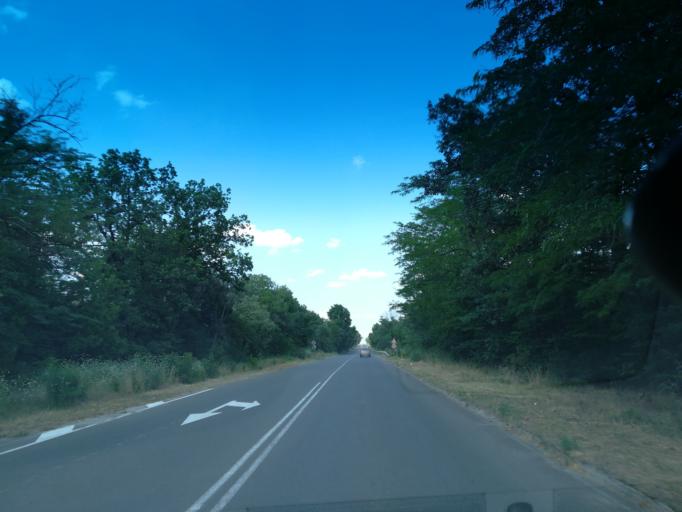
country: BG
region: Stara Zagora
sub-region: Obshtina Chirpan
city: Chirpan
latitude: 42.2040
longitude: 25.3480
